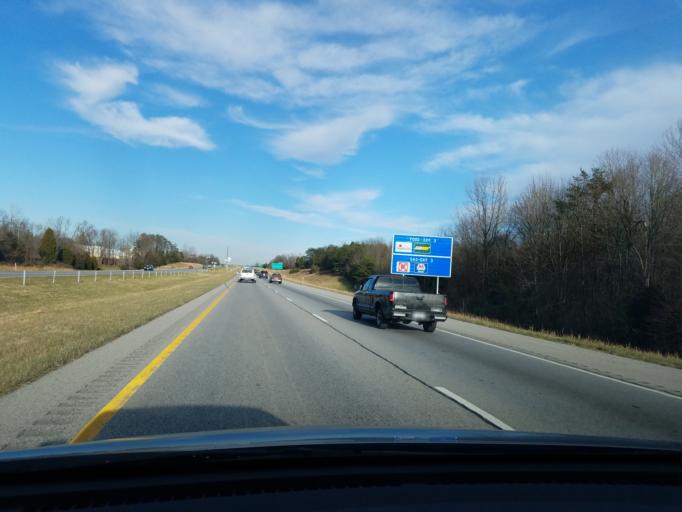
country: US
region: Indiana
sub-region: Floyd County
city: New Albany
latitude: 38.3263
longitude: -85.8339
